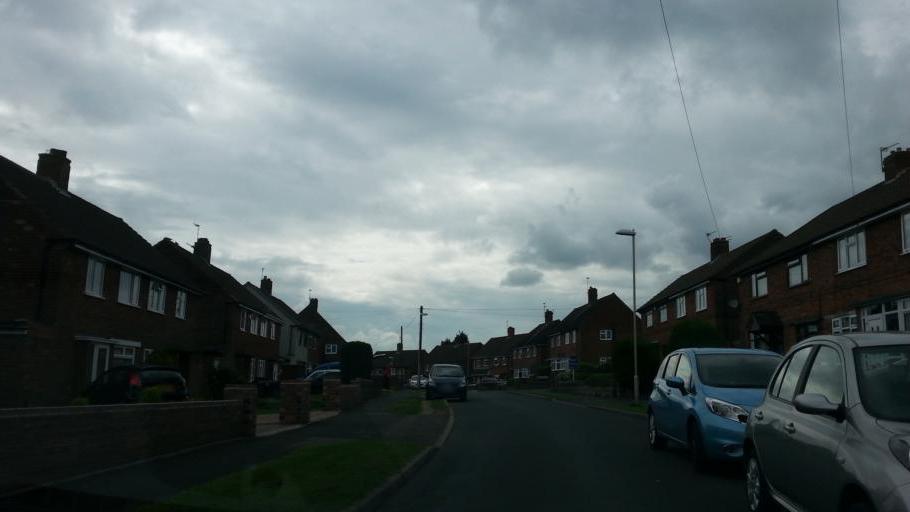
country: GB
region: England
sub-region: Sandwell
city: Tipton
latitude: 52.5352
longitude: -2.0898
